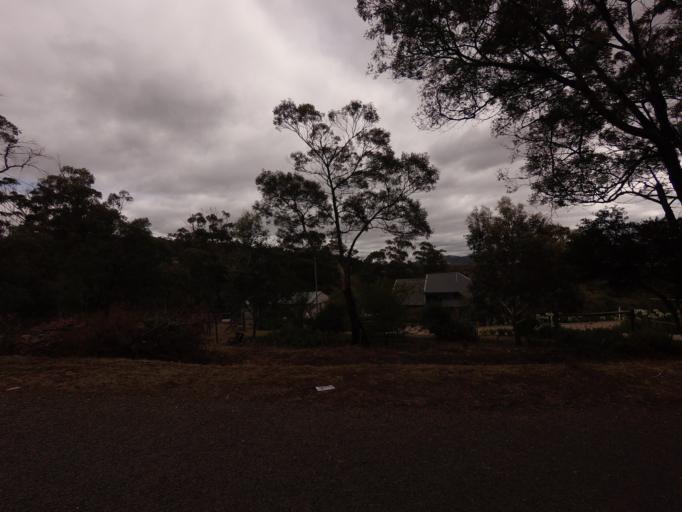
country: AU
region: Tasmania
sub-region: Clarence
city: Cambridge
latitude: -42.7824
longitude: 147.4086
